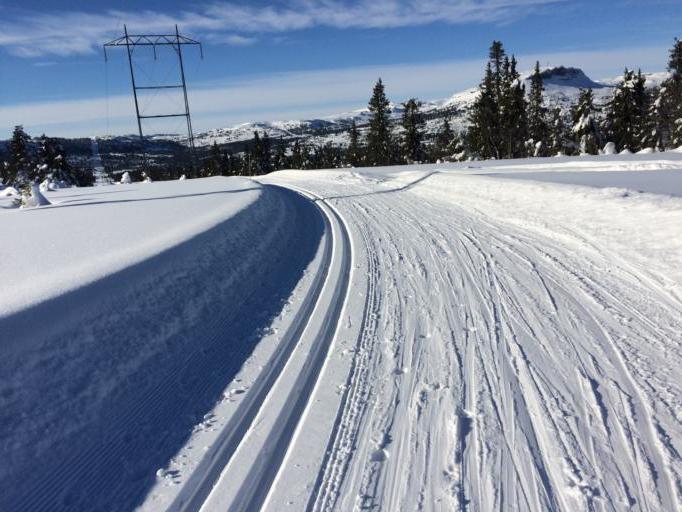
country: NO
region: Oppland
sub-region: Gausdal
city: Segalstad bru
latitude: 61.3135
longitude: 10.1063
